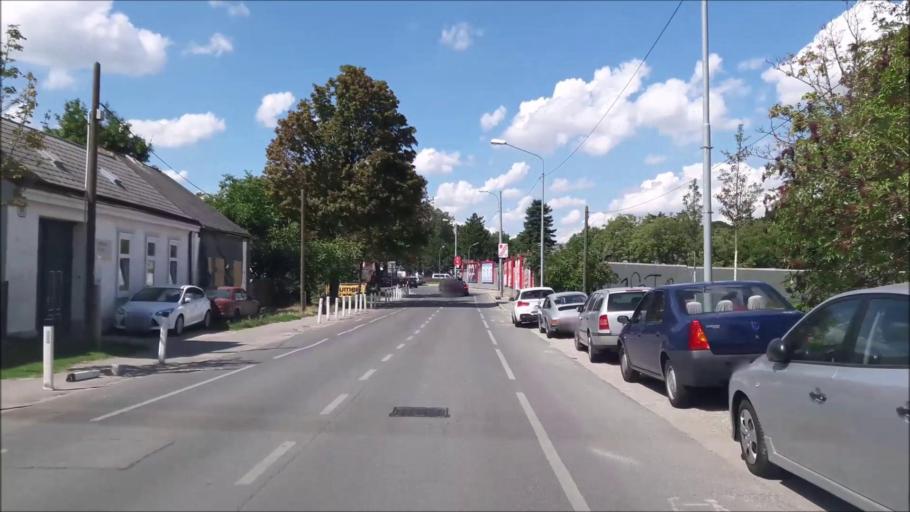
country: AT
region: Lower Austria
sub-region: Politischer Bezirk Wien-Umgebung
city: Gerasdorf bei Wien
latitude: 48.2335
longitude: 16.4676
